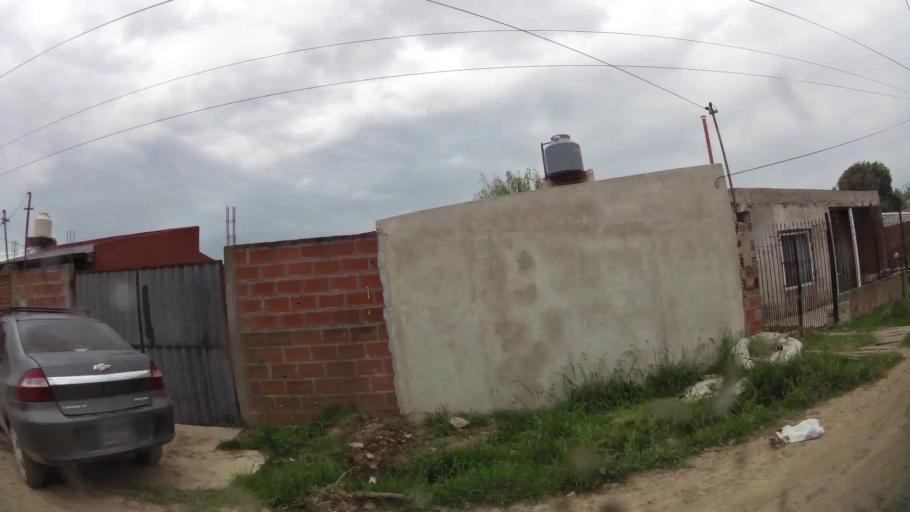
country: AR
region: Buenos Aires
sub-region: Partido de Zarate
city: Zarate
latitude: -34.1094
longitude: -59.0377
